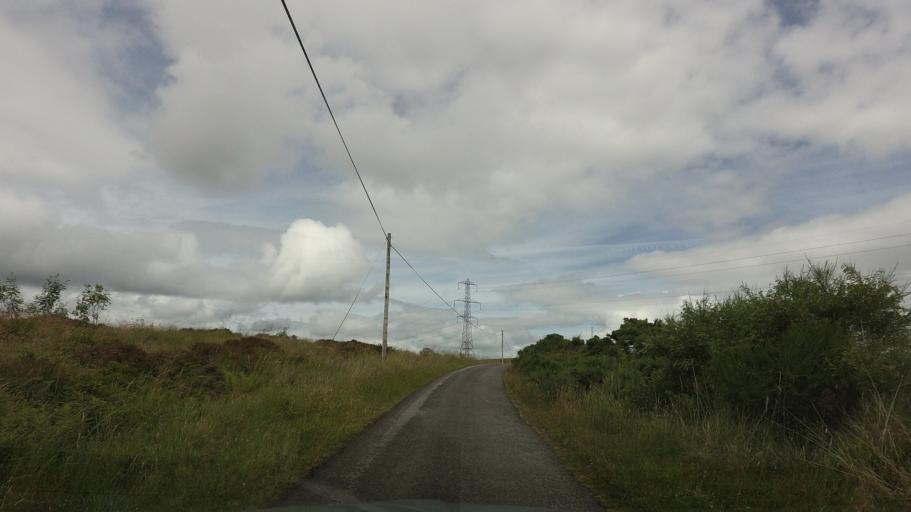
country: GB
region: Scotland
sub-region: Stirling
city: Killearn
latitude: 56.0959
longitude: -4.4310
